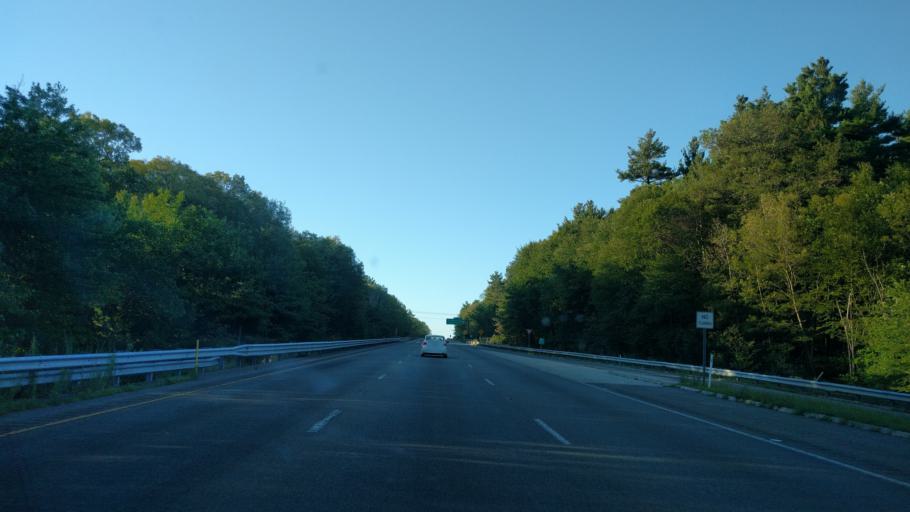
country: US
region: Massachusetts
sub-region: Middlesex County
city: Hopkinton
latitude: 42.2155
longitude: -71.5474
